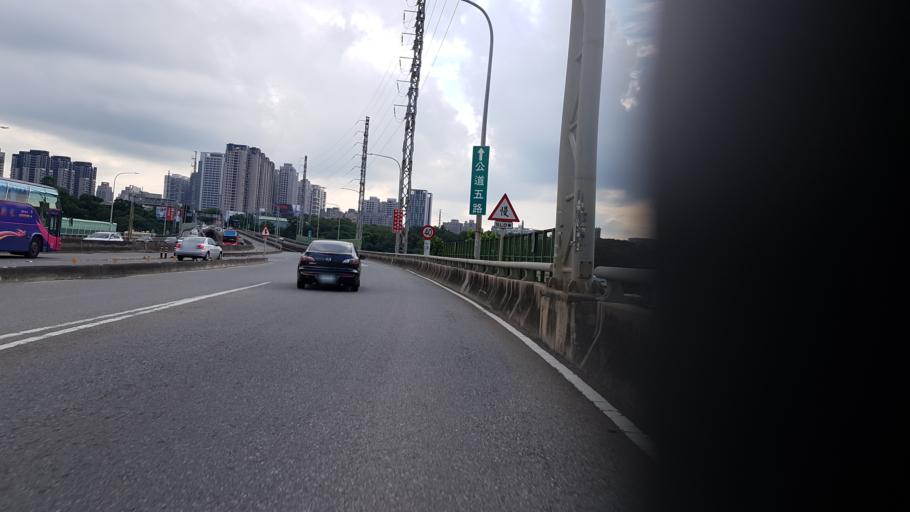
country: TW
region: Taiwan
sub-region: Hsinchu
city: Zhubei
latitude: 24.8022
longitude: 121.0141
